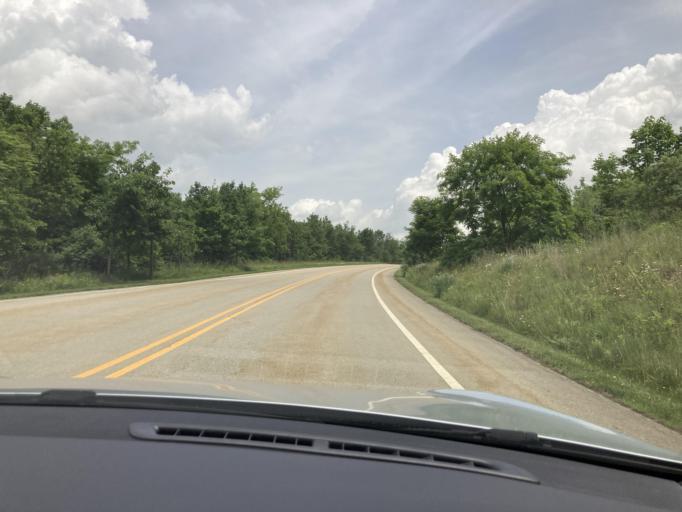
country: US
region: Pennsylvania
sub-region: Somerset County
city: Friedens
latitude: 40.0619
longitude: -78.9061
